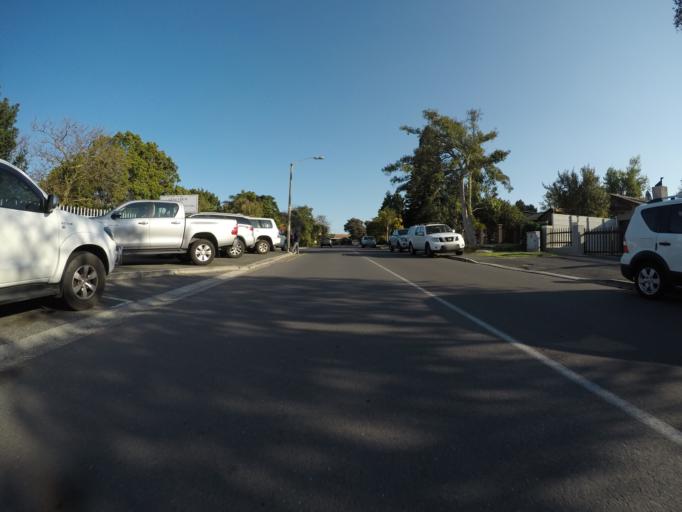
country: ZA
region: Western Cape
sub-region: City of Cape Town
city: Kraaifontein
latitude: -33.8542
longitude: 18.6575
